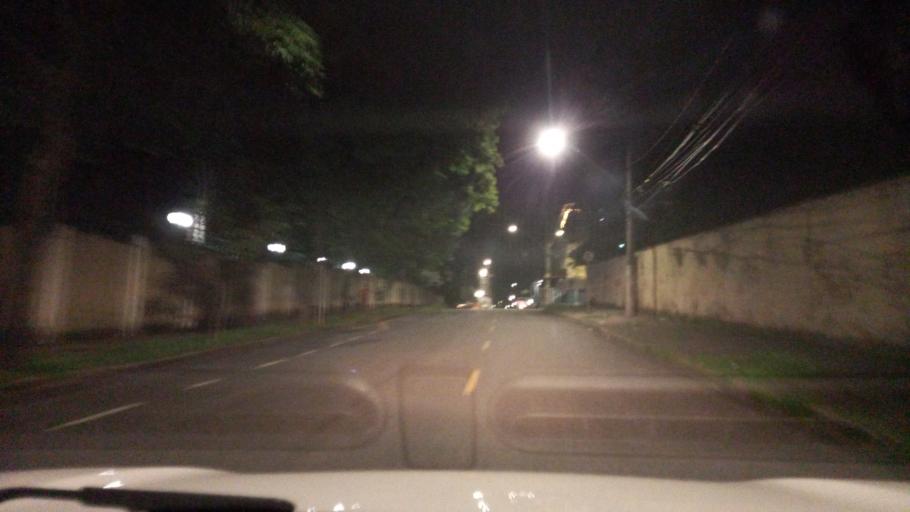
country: BR
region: Minas Gerais
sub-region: Belo Horizonte
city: Belo Horizonte
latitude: -19.8586
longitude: -43.9197
